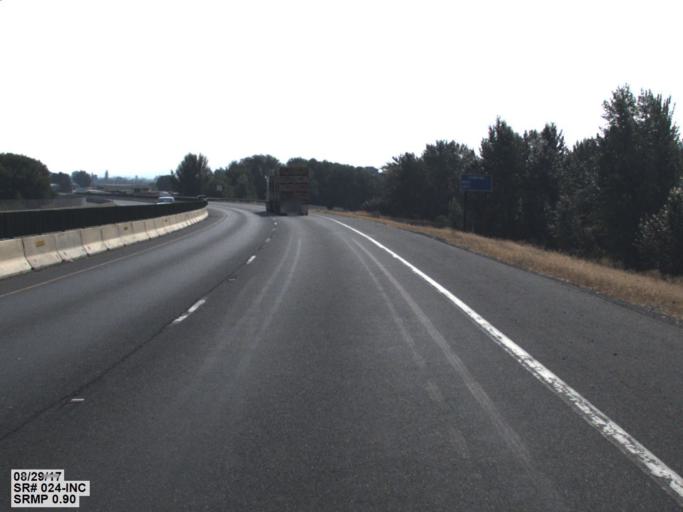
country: US
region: Washington
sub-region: Yakima County
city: Union Gap
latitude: 46.5785
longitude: -120.4590
